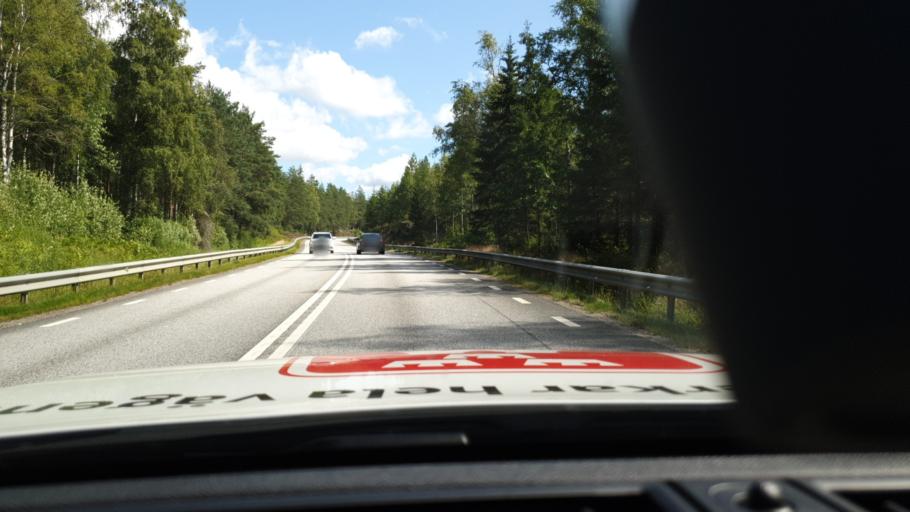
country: SE
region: Joenkoeping
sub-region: Eksjo Kommun
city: Haljarp
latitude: 57.6208
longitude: 15.4852
